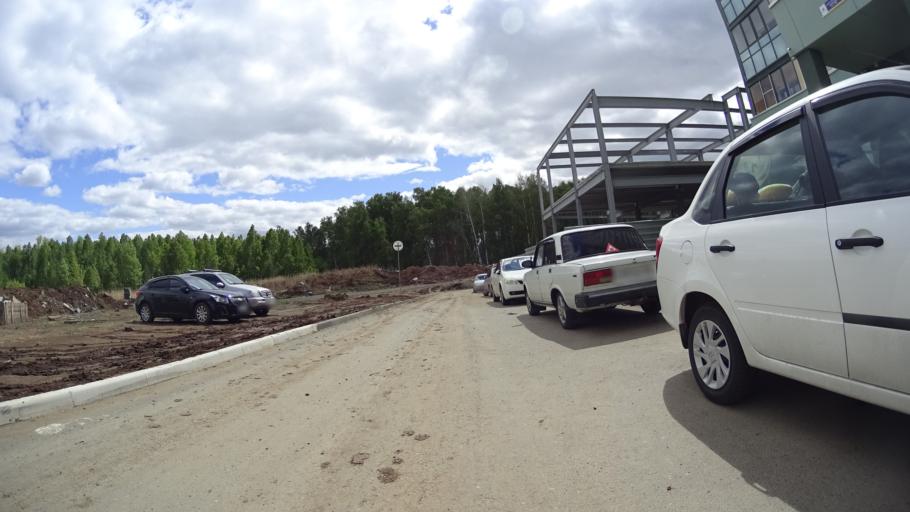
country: RU
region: Chelyabinsk
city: Roshchino
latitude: 55.1717
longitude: 61.2563
